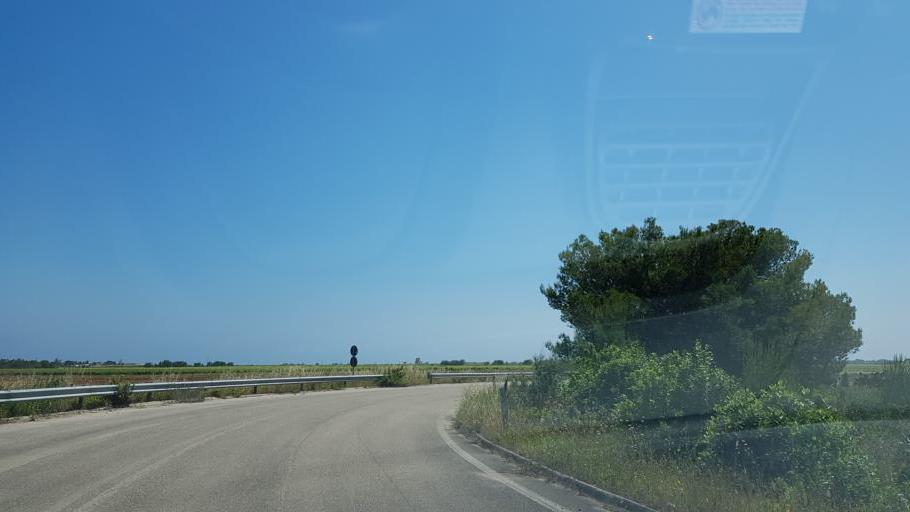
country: IT
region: Apulia
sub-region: Provincia di Brindisi
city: Brindisi
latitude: 40.6701
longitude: 17.8611
